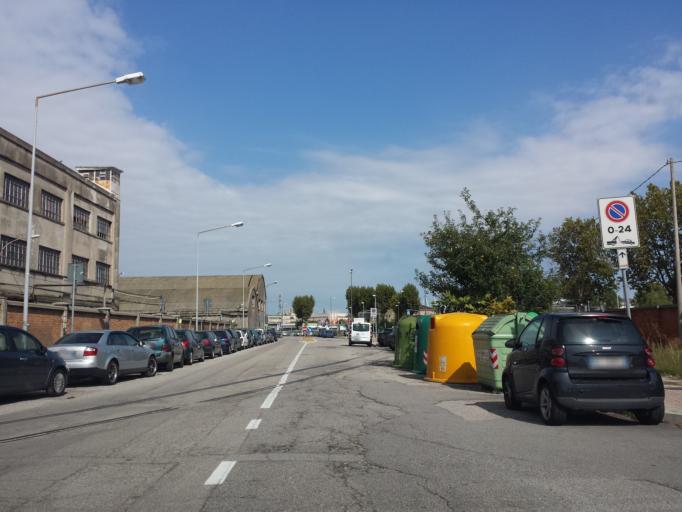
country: IT
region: Veneto
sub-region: Provincia di Venezia
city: Mestre
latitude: 45.4743
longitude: 12.2513
